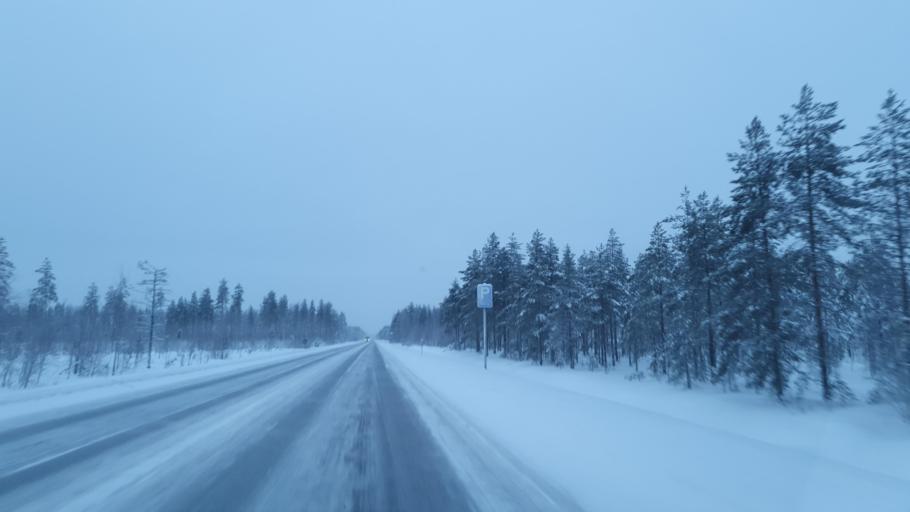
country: FI
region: Kainuu
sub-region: Kajaani
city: Vaala
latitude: 64.5972
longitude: 26.7584
